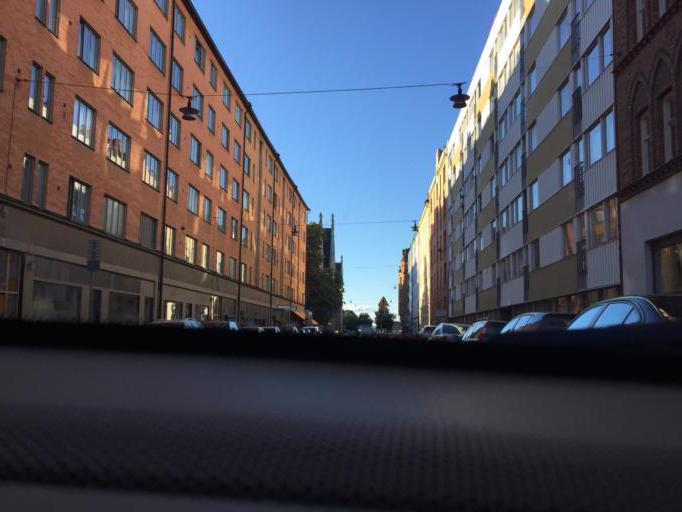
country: SE
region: Stockholm
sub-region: Stockholms Kommun
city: Stockholm
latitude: 59.3494
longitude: 18.0571
